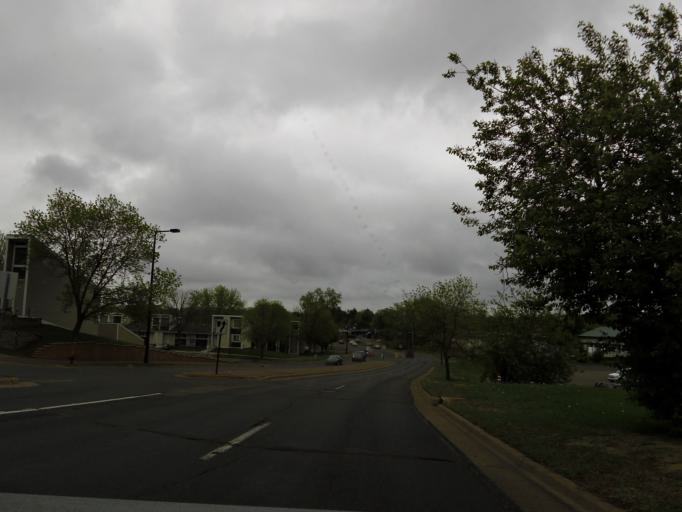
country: US
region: Minnesota
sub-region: Washington County
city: Stillwater
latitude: 45.0414
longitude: -92.8253
